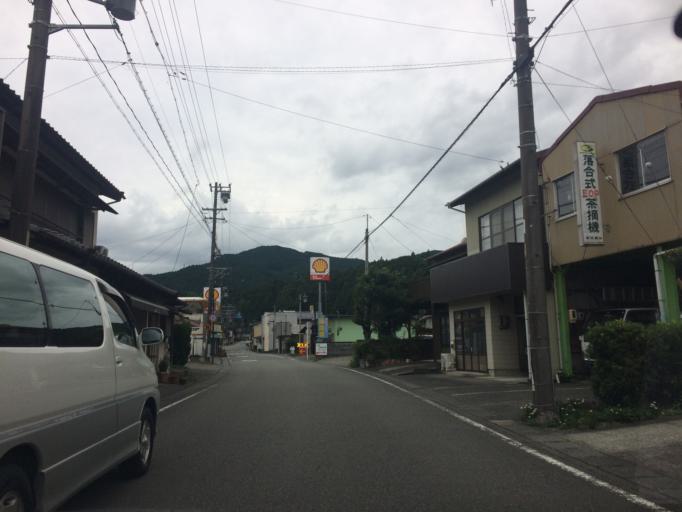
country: JP
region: Shizuoka
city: Kanaya
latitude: 35.0421
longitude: 138.0820
